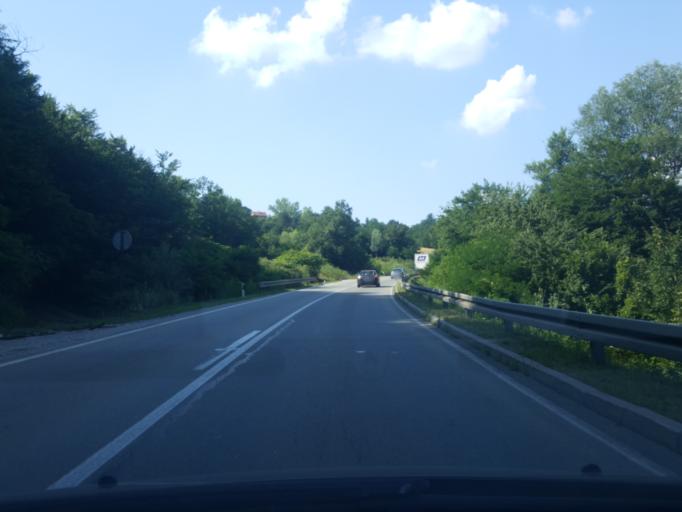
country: RS
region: Central Serbia
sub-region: Moravicki Okrug
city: Gornji Milanovac
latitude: 44.1100
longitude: 20.4832
